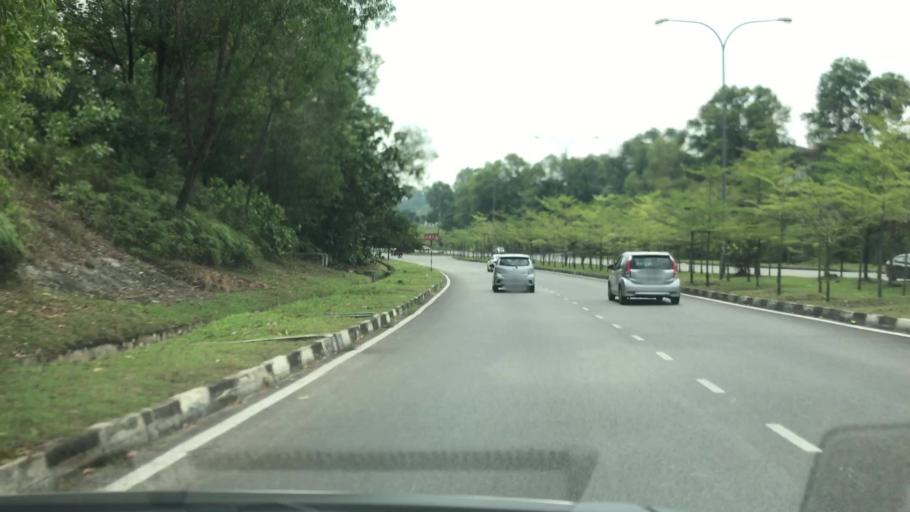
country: MY
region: Putrajaya
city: Putrajaya
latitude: 3.0059
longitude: 101.6692
